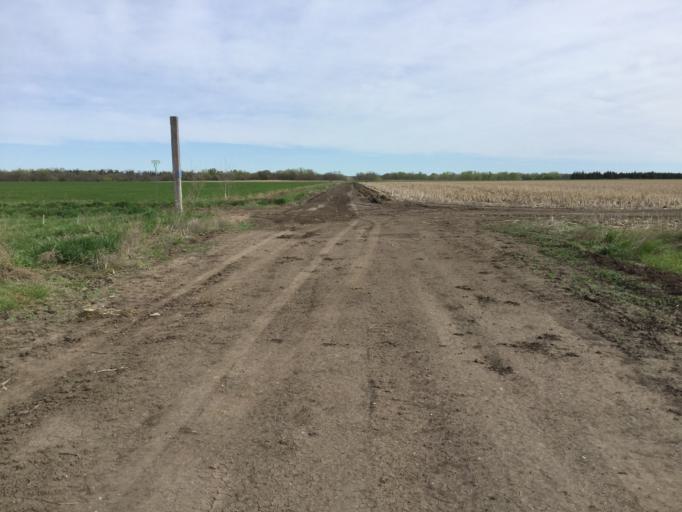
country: US
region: Kansas
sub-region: Osborne County
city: Osborne
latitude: 39.4153
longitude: -98.5922
